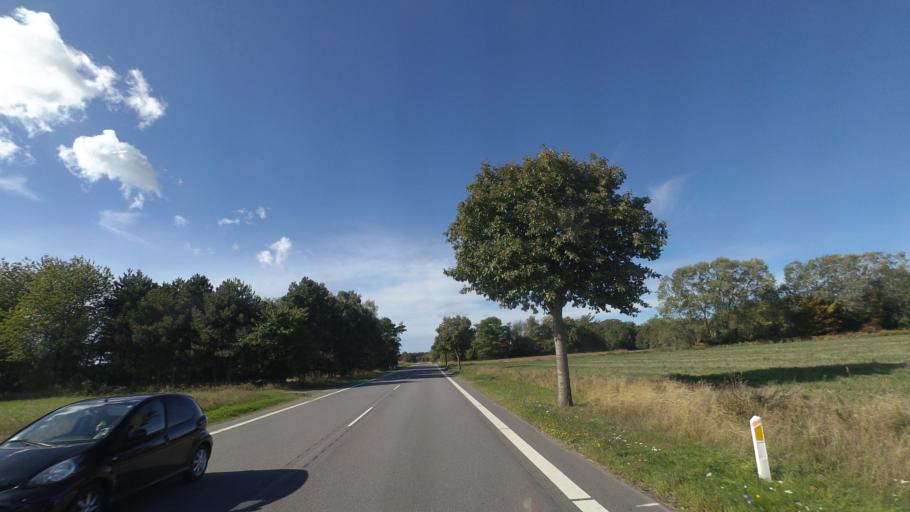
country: DK
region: Capital Region
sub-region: Bornholm Kommune
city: Ronne
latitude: 55.0766
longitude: 14.7731
